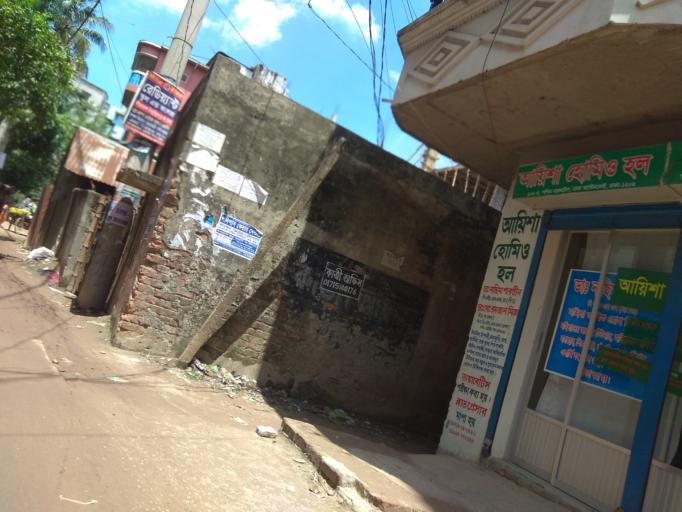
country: BD
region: Dhaka
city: Tungi
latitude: 23.8309
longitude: 90.3854
